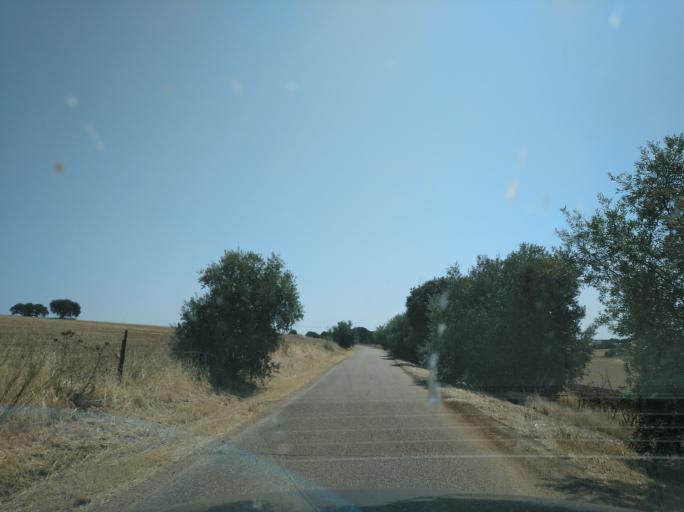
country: PT
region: Portalegre
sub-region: Campo Maior
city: Campo Maior
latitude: 39.0311
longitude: -7.0064
